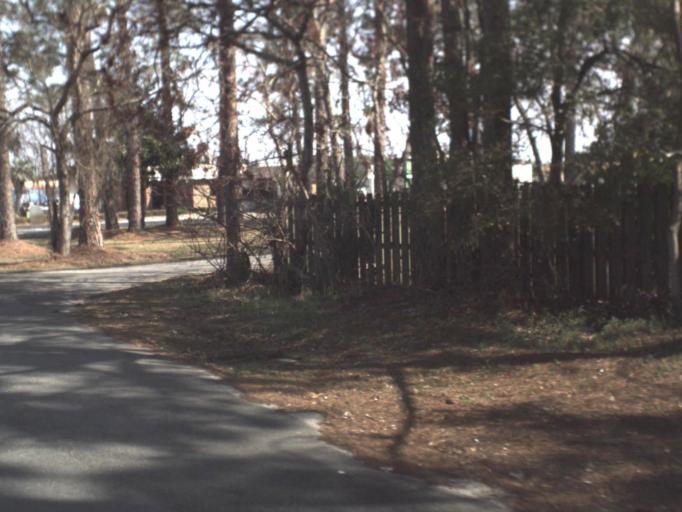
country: US
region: Florida
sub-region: Bay County
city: Pretty Bayou
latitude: 30.1886
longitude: -85.7010
